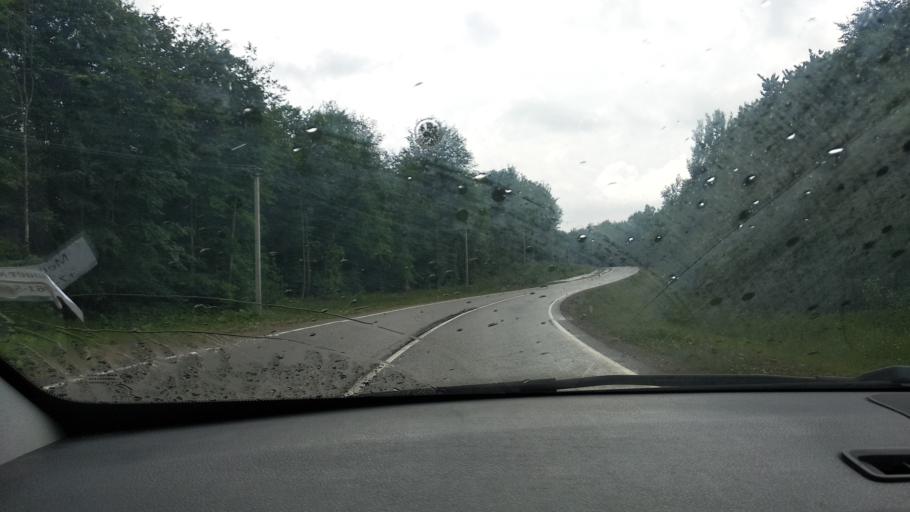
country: RU
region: Adygeya
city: Kamennomostskiy
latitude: 44.2332
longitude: 39.9882
